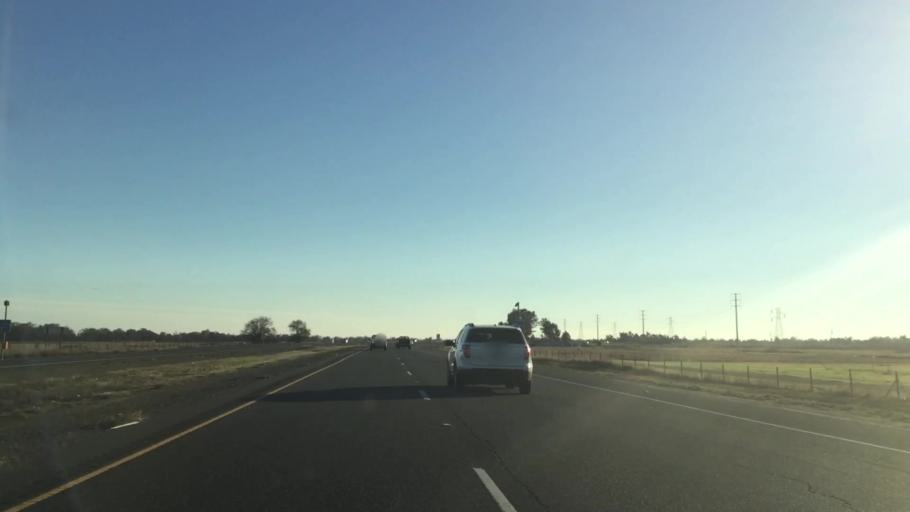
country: US
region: California
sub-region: Yuba County
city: Olivehurst
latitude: 39.0717
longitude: -121.5411
